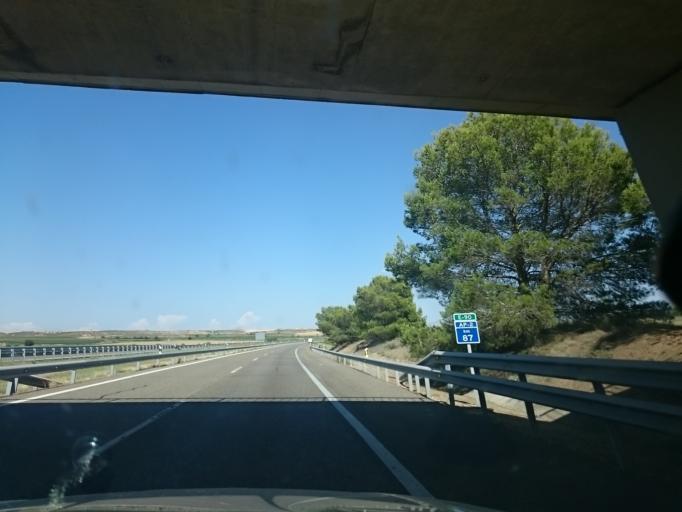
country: ES
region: Aragon
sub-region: Provincia de Huesca
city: Candasnos
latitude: 41.5235
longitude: 0.0512
